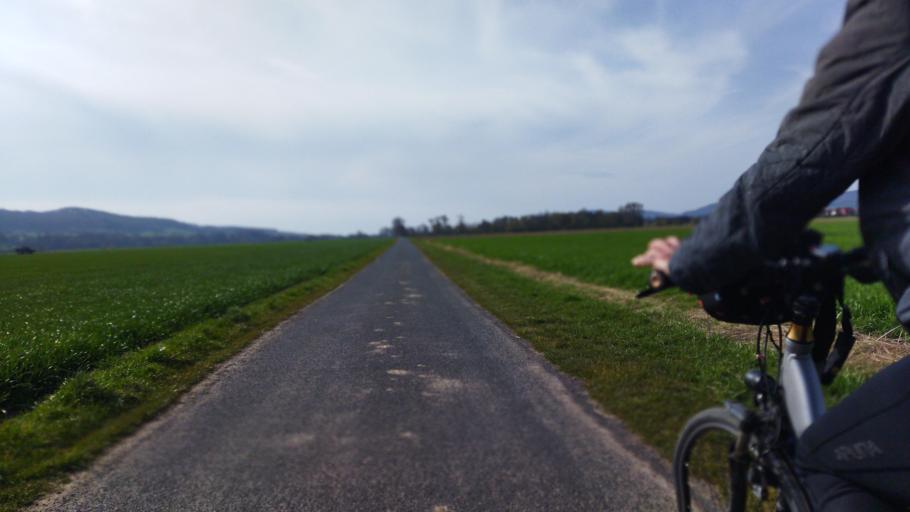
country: DE
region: Lower Saxony
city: Hessisch Oldendorf
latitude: 52.1645
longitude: 9.2098
